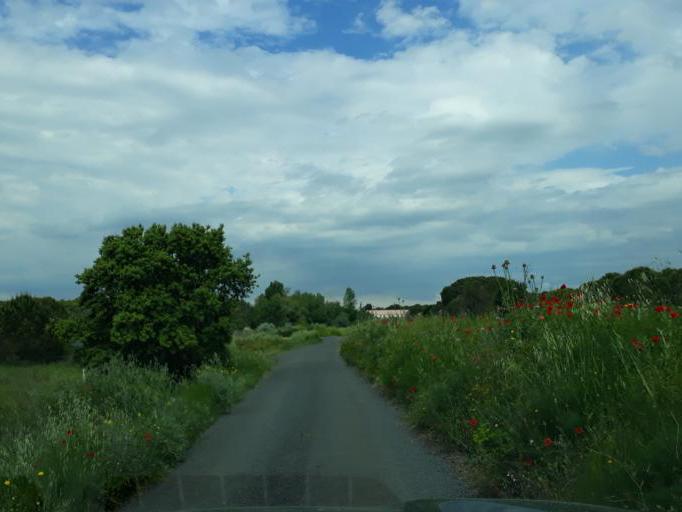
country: FR
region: Languedoc-Roussillon
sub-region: Departement de l'Herault
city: Agde
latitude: 43.2910
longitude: 3.4876
